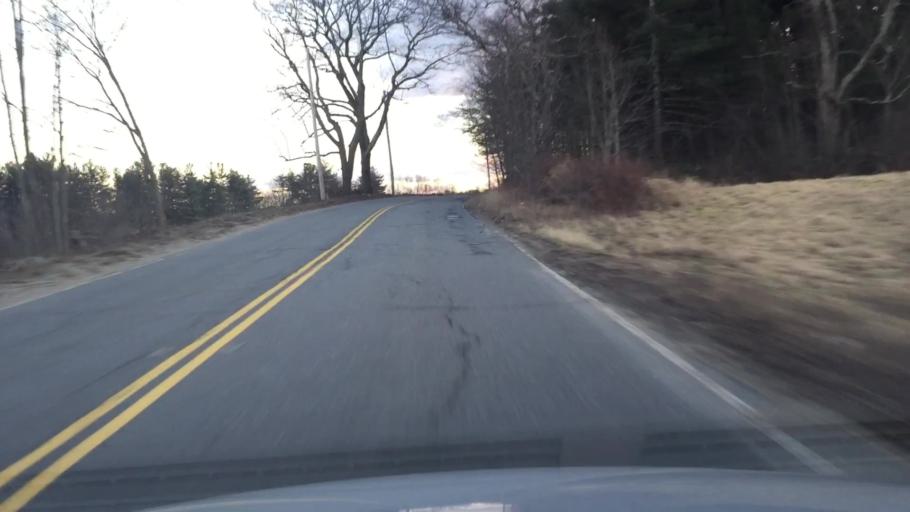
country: US
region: Massachusetts
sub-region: Worcester County
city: Sterling
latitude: 42.4211
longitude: -71.8073
